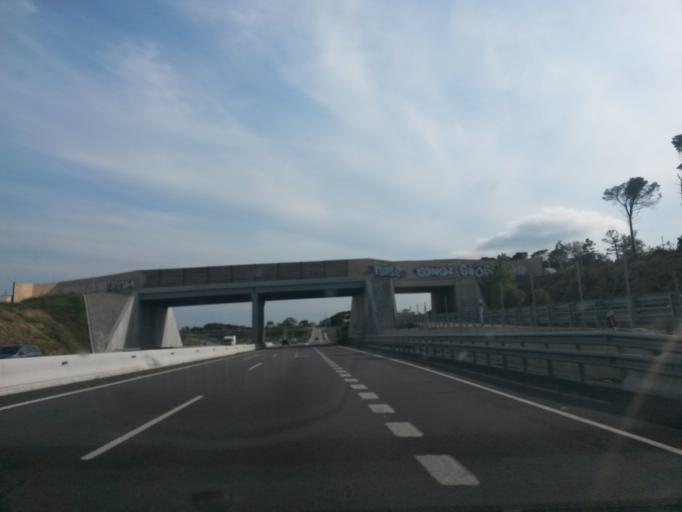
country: ES
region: Catalonia
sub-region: Provincia de Girona
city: Sils
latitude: 41.8384
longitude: 2.7593
